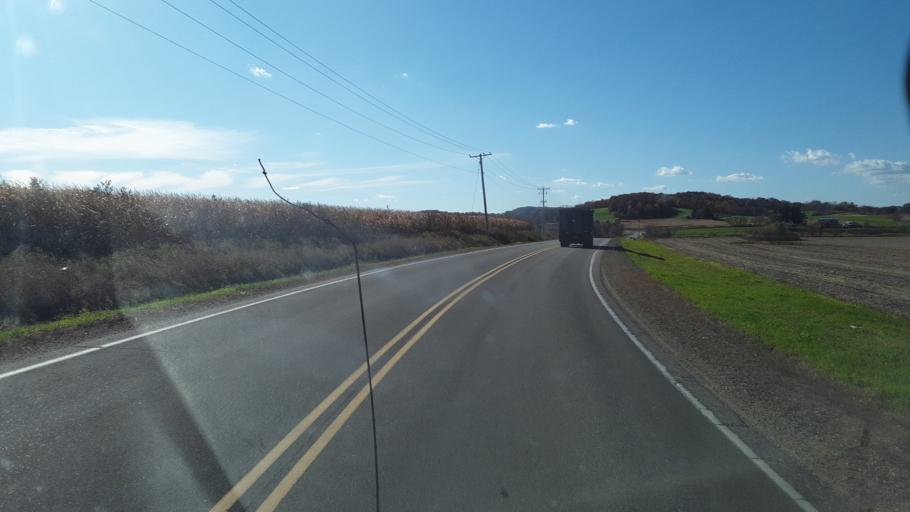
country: US
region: Wisconsin
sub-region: Sauk County
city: Reedsburg
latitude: 43.5405
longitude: -90.1601
